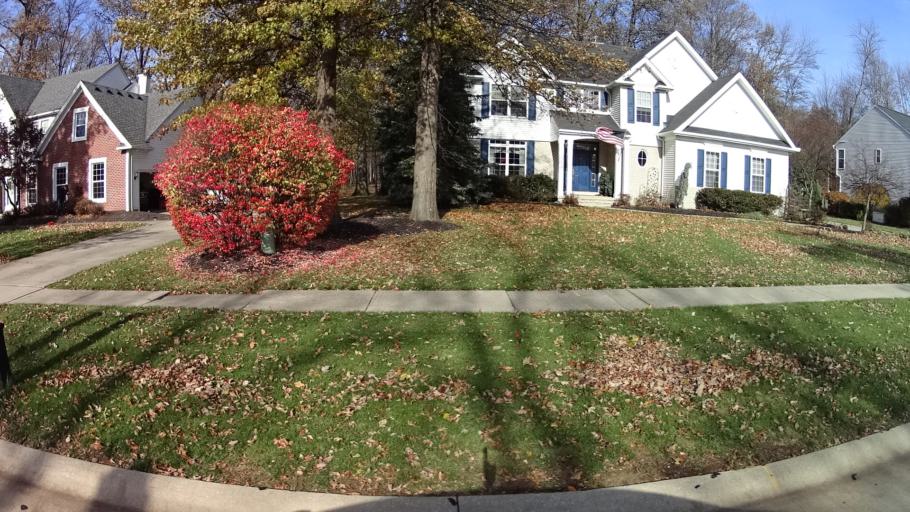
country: US
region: Ohio
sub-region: Lorain County
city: Avon Lake
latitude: 41.5045
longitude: -81.9956
